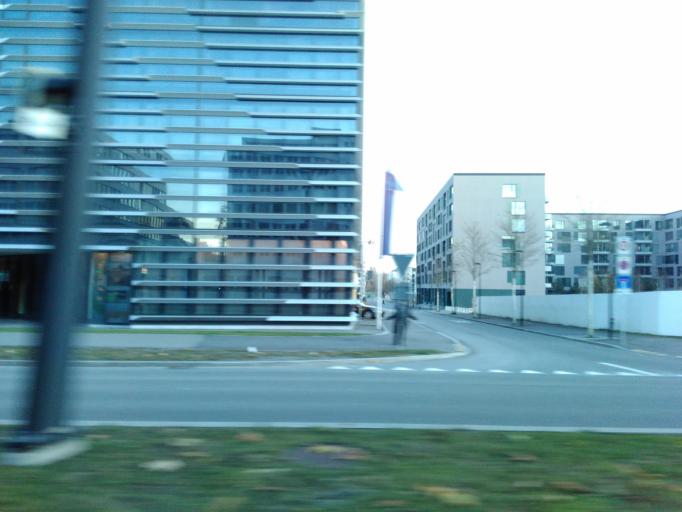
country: CH
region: Zurich
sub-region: Bezirk Buelach
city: Glattbrugg
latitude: 47.4227
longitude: 8.5586
